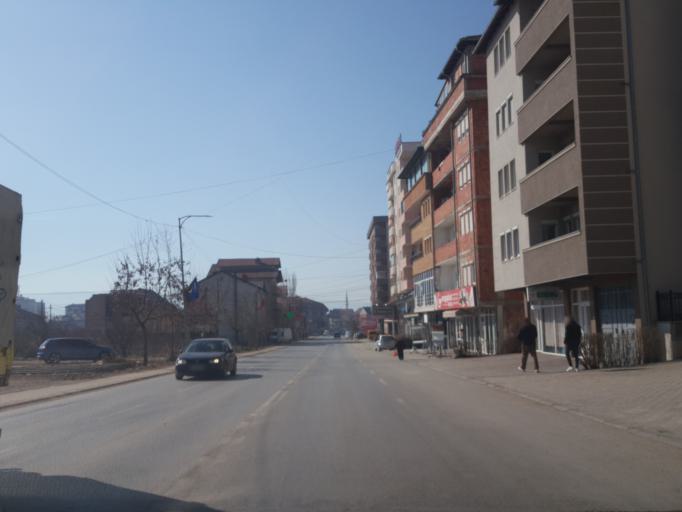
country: XK
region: Mitrovica
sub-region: Vushtrri
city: Vushtrri
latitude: 42.8265
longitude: 20.9699
